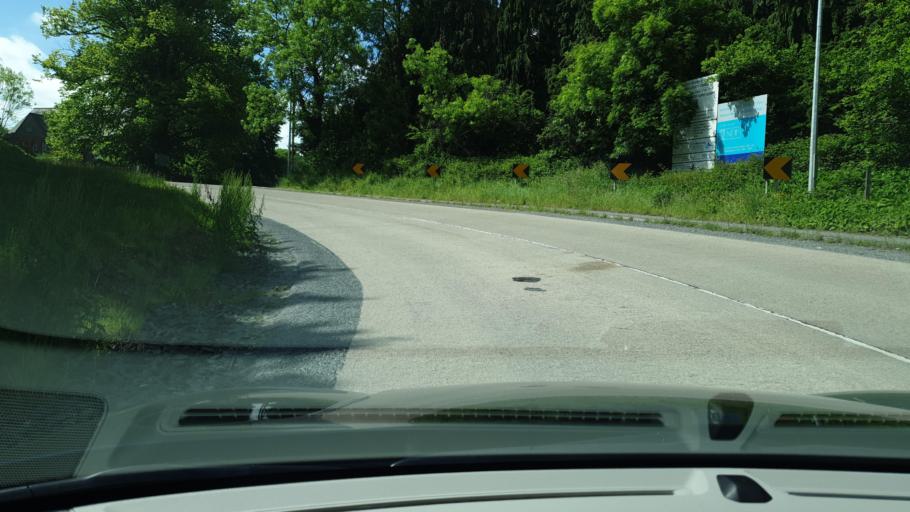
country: IE
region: Ulster
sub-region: An Cabhan
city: Kingscourt
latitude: 53.9059
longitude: -6.7975
